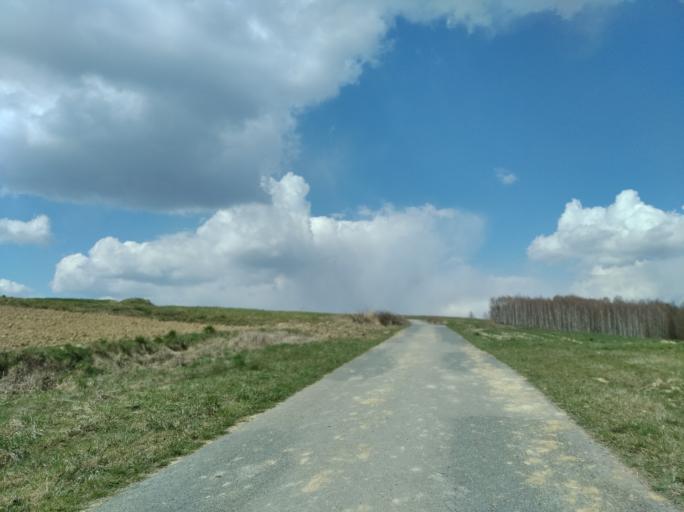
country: PL
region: Subcarpathian Voivodeship
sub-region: Powiat strzyzowski
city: Strzyzow
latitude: 49.9151
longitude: 21.7297
